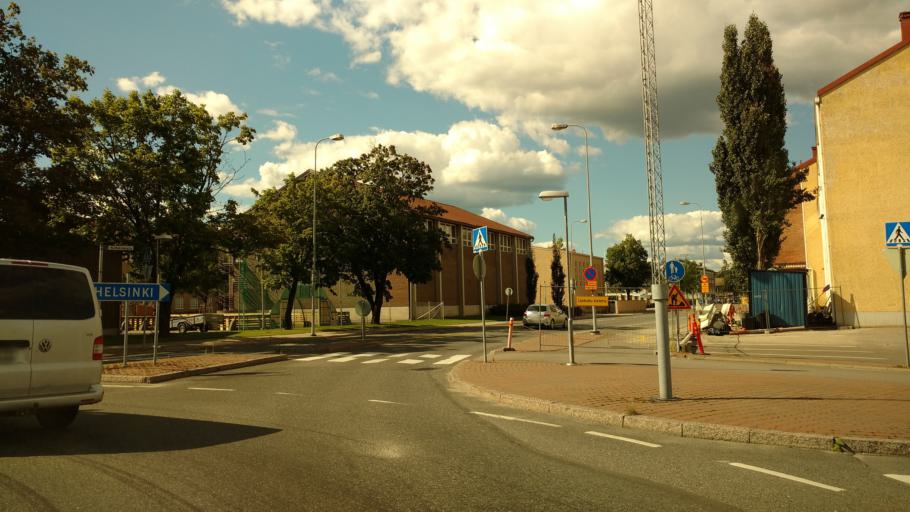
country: FI
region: Varsinais-Suomi
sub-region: Salo
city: Salo
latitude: 60.3839
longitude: 23.1341
